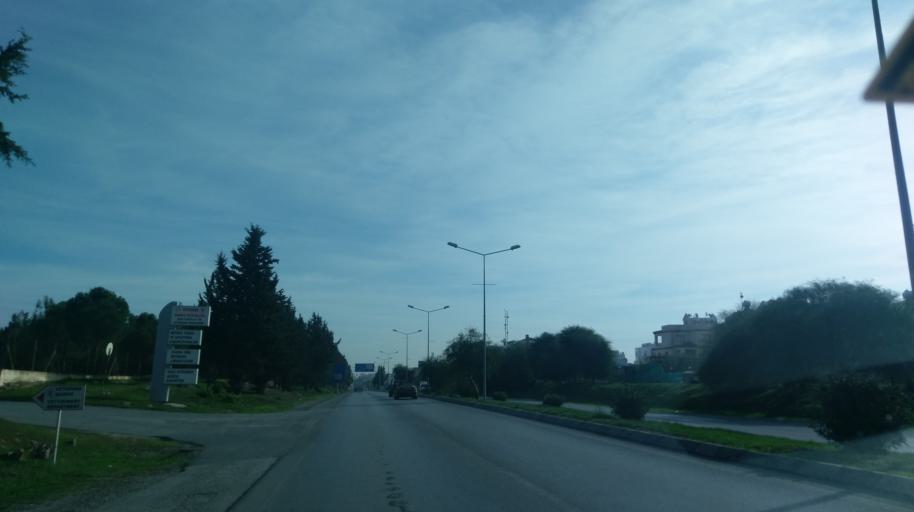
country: CY
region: Lefkosia
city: Nicosia
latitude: 35.2099
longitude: 33.3612
